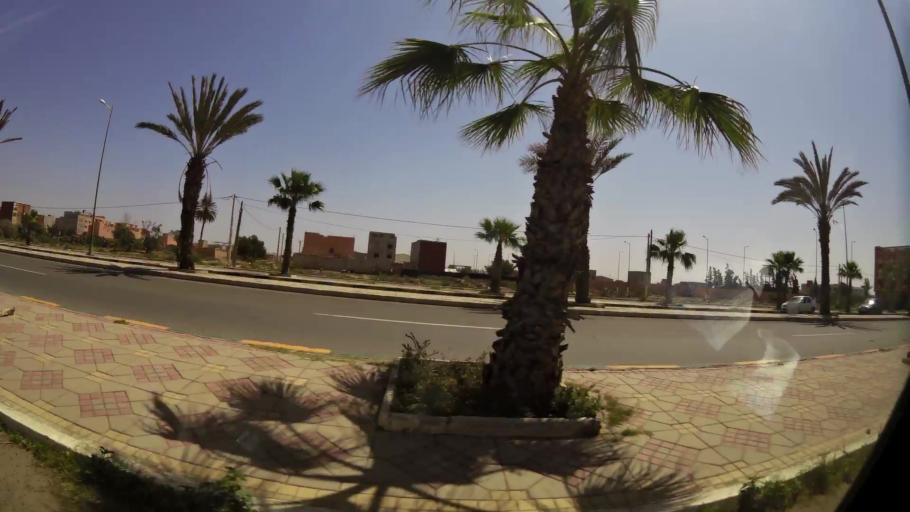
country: MA
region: Souss-Massa-Draa
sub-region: Inezgane-Ait Mellou
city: Inezgane
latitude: 30.3188
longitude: -9.5033
